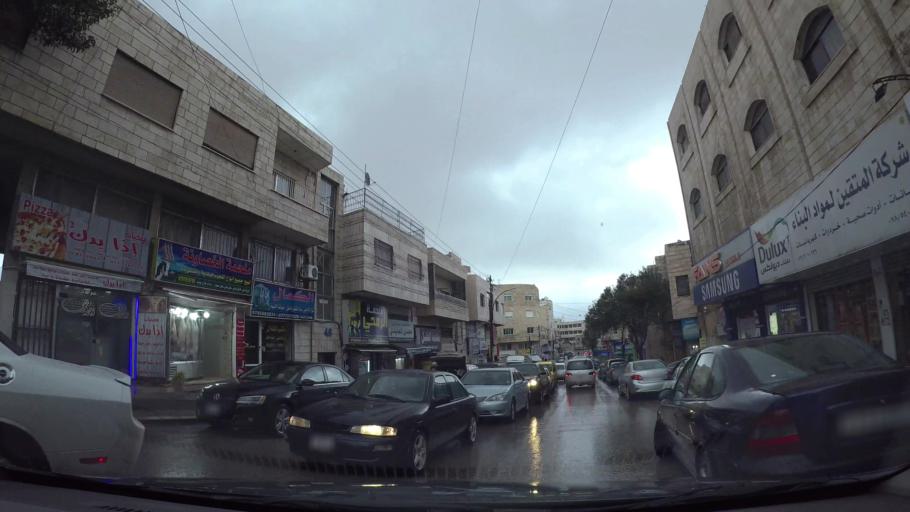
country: JO
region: Amman
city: Al Jubayhah
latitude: 32.0250
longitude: 35.8647
